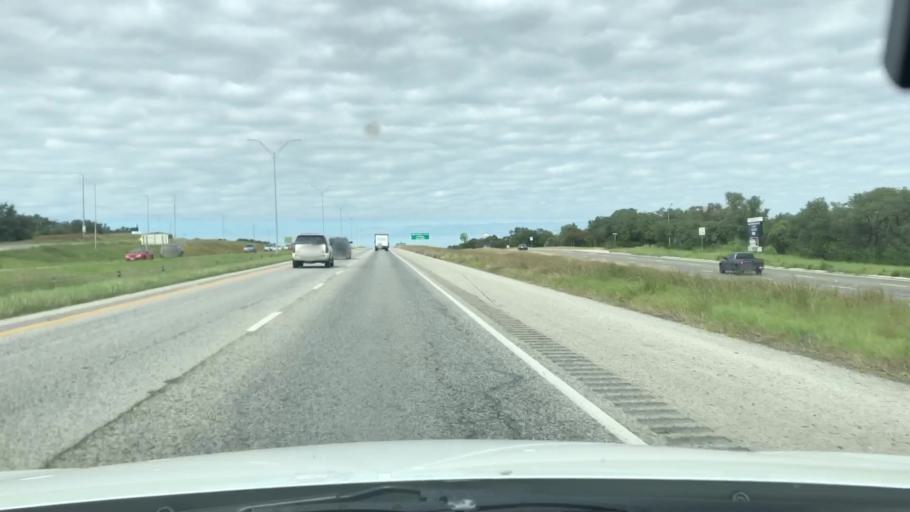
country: US
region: Texas
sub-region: Bexar County
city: Leon Valley
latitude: 29.4535
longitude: -98.6867
